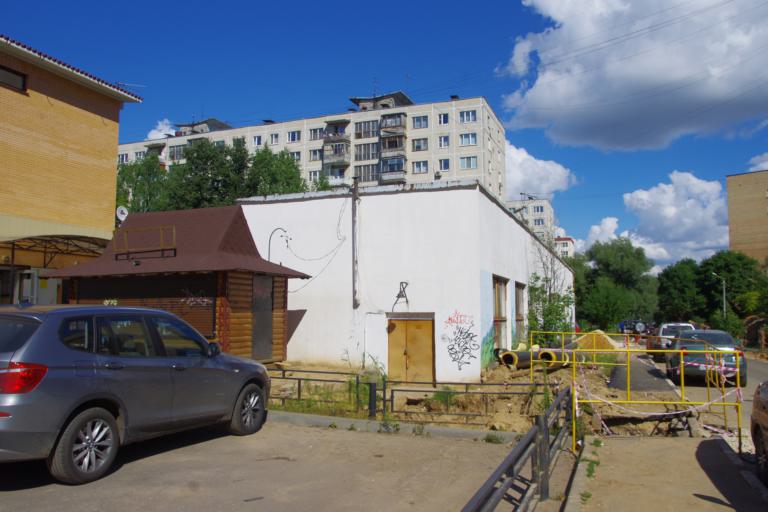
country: RU
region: Moskovskaya
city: Krasnogorsk
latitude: 55.8377
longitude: 37.3012
